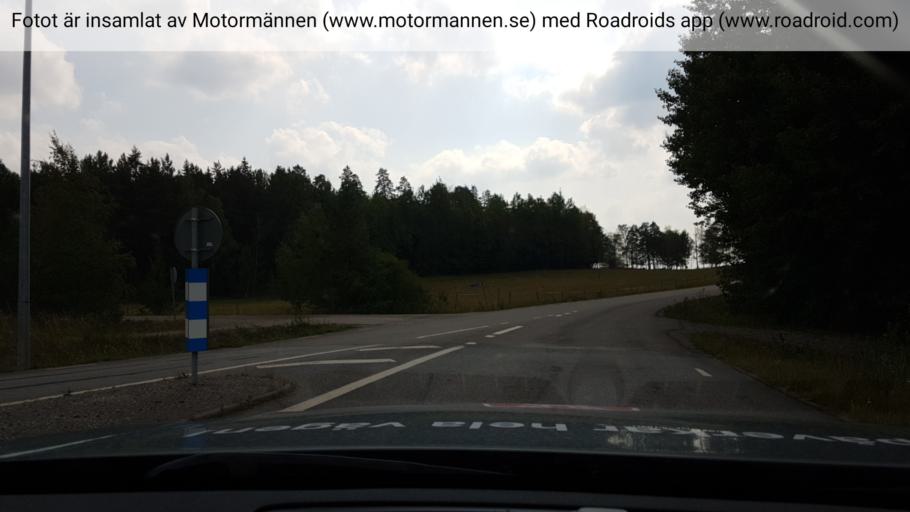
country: SE
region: Soedermanland
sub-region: Gnesta Kommun
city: Gnesta
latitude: 59.0467
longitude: 17.2795
